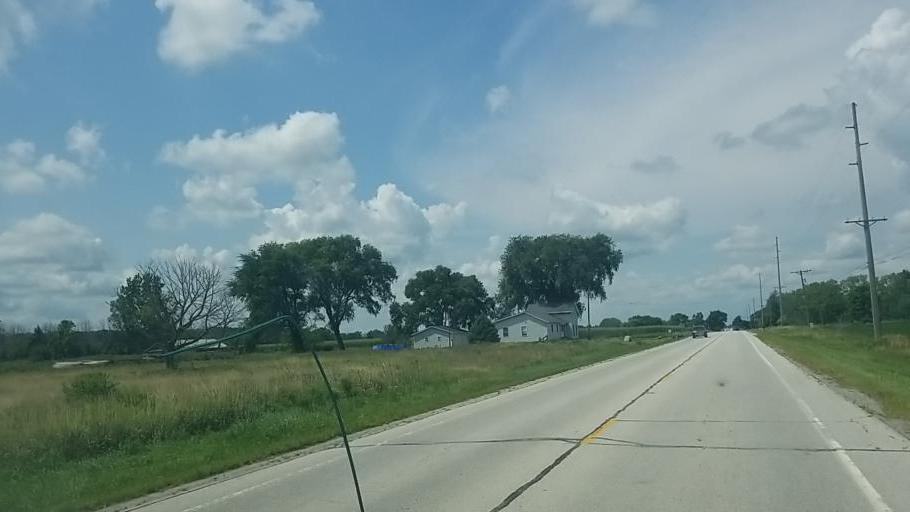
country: US
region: Ohio
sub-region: Wayne County
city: West Salem
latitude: 41.0273
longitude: -82.1309
